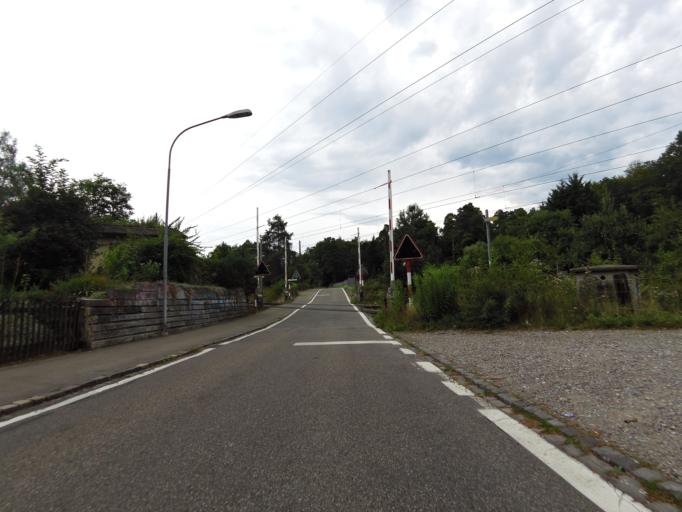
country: CH
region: Zurich
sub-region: Bezirk Zuerich
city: Zuerich (Kreis 11) / Affoltern
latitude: 47.4182
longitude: 8.5154
